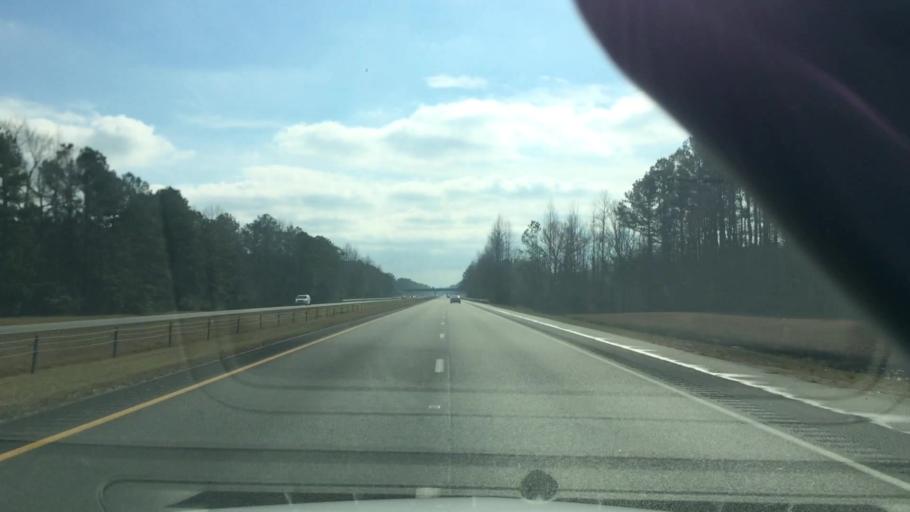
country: US
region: North Carolina
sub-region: Pender County
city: Rocky Point
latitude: 34.4869
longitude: -77.8781
